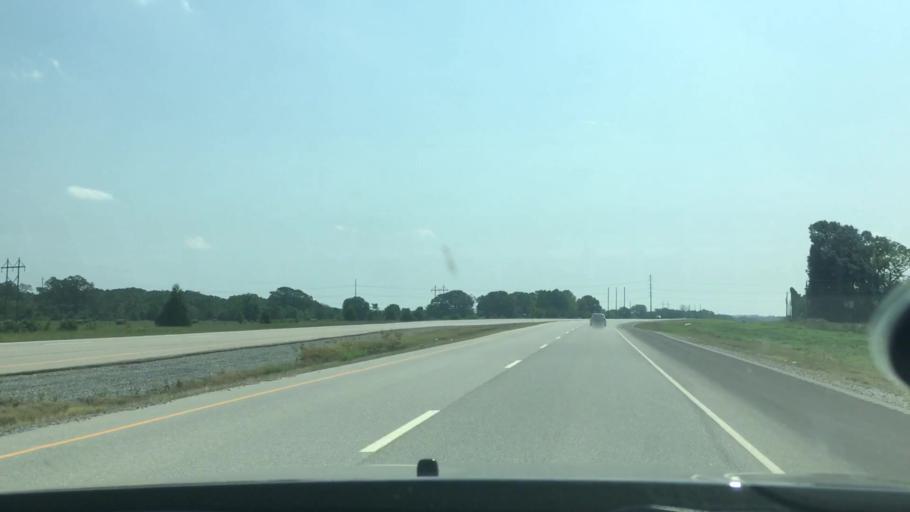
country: US
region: Oklahoma
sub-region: Atoka County
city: Atoka
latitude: 34.3361
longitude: -96.0578
